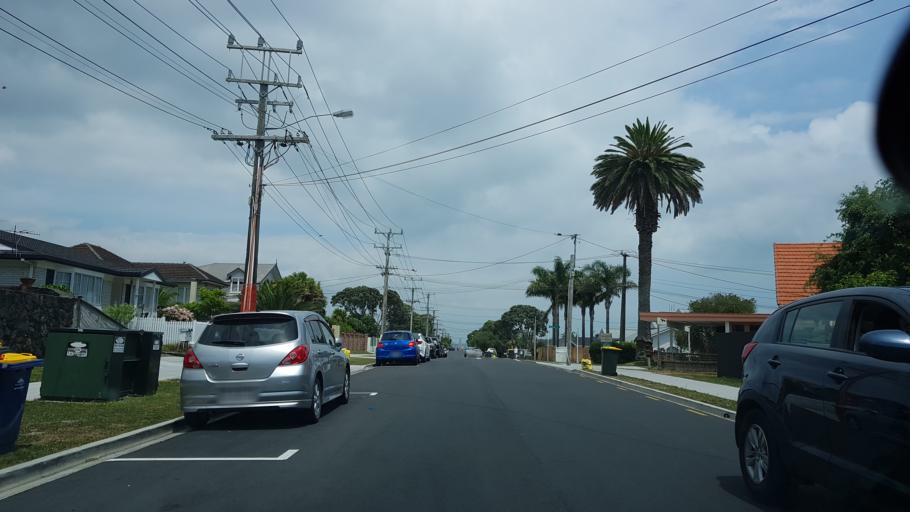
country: NZ
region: Auckland
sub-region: Auckland
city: North Shore
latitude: -36.7984
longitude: 174.7782
